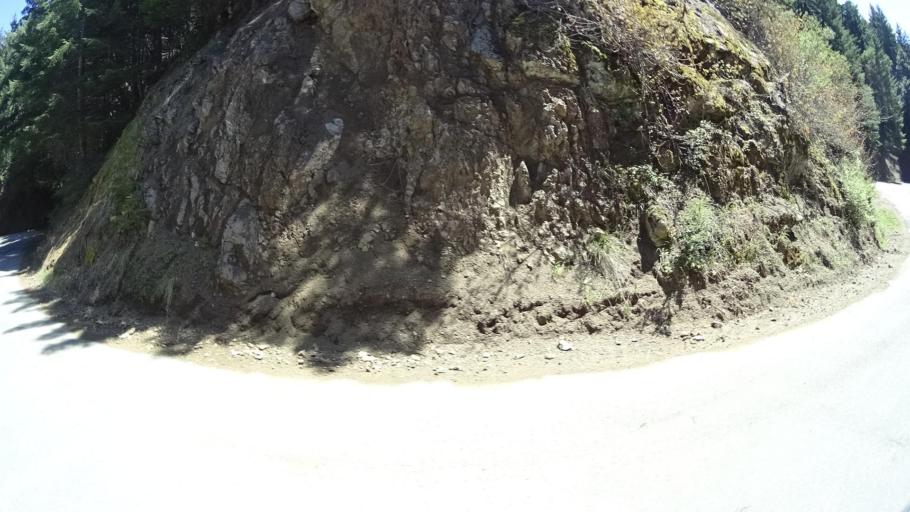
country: US
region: California
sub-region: Humboldt County
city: Rio Dell
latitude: 40.2844
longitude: -124.0638
